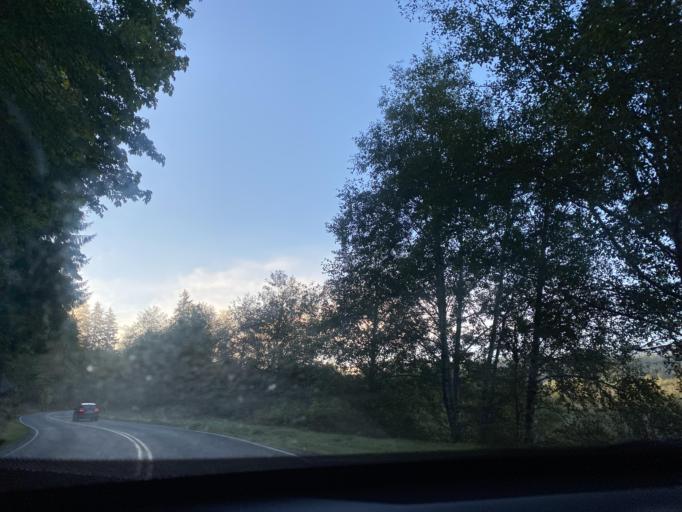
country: US
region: Washington
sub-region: Clallam County
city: Forks
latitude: 47.8200
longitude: -124.1785
